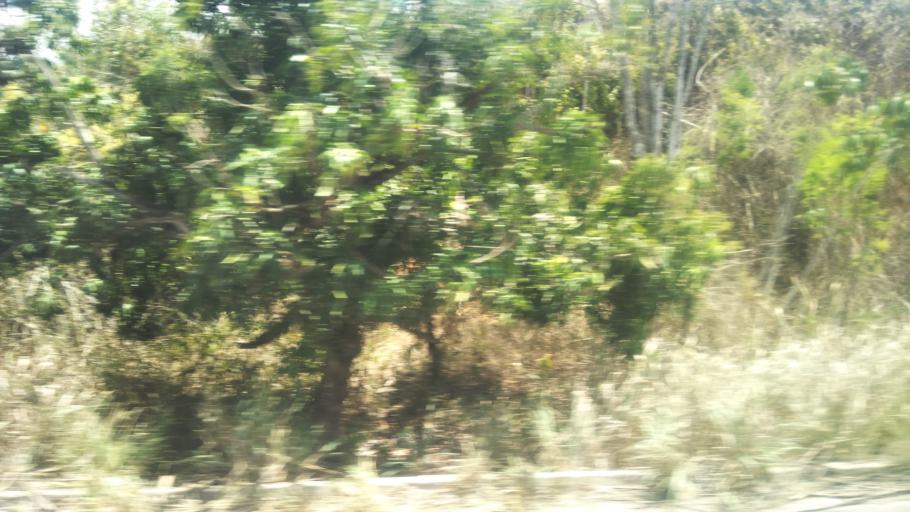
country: BR
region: Pernambuco
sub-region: Nazare Da Mata
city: Nazare da Mata
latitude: -7.7375
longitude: -35.2886
